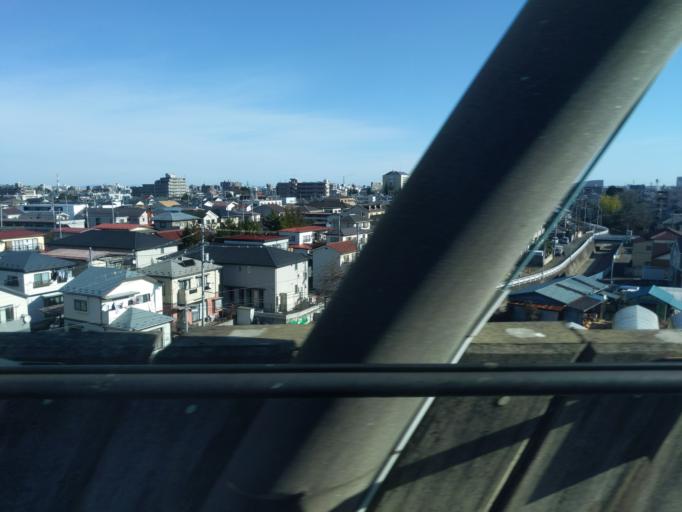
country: JP
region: Miyagi
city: Sendai
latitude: 38.2437
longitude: 140.8933
